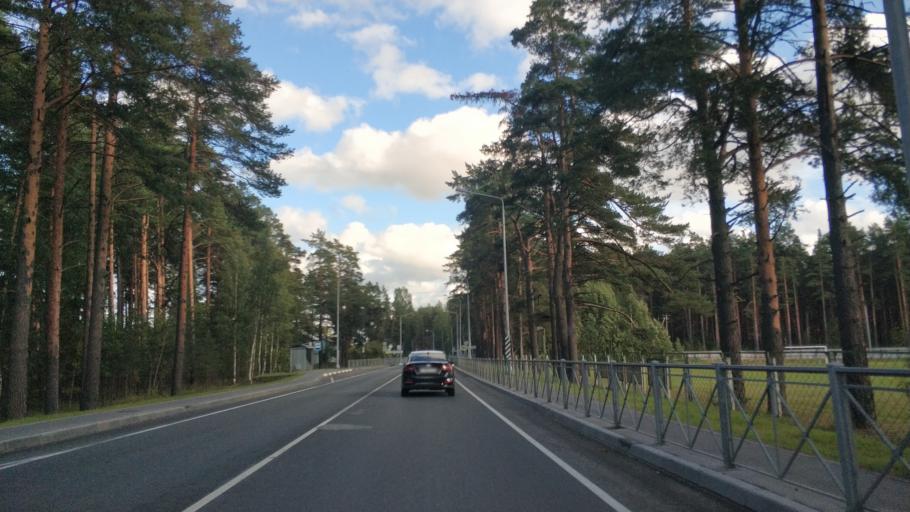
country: RU
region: Leningrad
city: Priozersk
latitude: 61.0185
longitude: 30.1364
